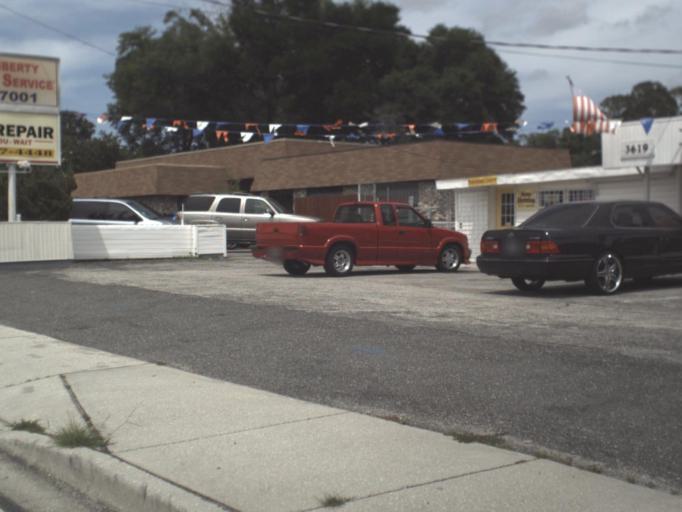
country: US
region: Florida
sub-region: Clay County
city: Bellair-Meadowbrook Terrace
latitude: 30.2699
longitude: -81.7362
